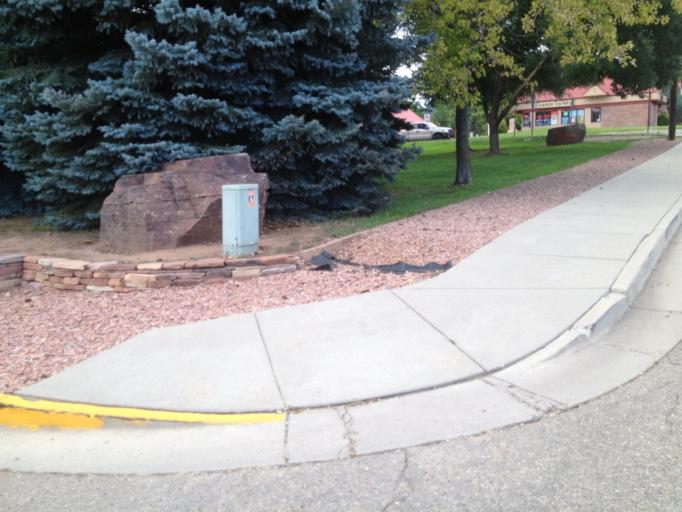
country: US
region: Colorado
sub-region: Boulder County
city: Lyons
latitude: 40.2236
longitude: -105.2676
